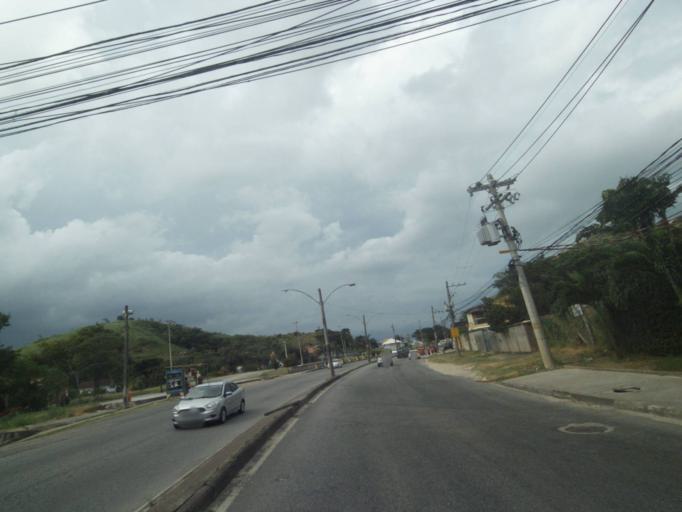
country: BR
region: Rio de Janeiro
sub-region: Nilopolis
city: Nilopolis
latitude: -22.8942
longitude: -43.3974
